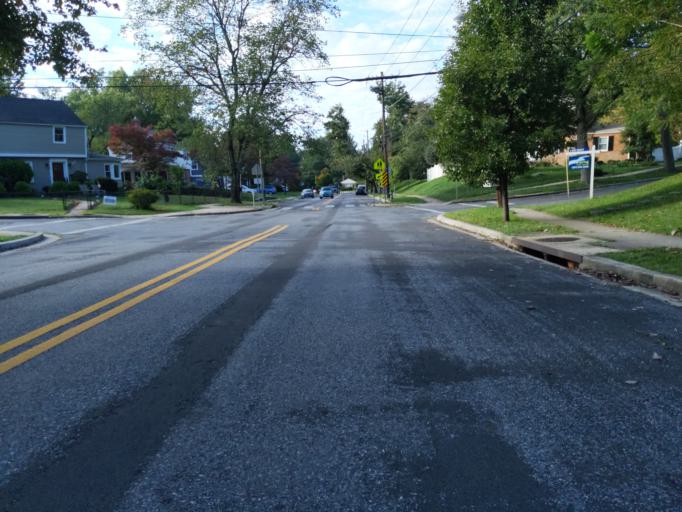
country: US
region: Maryland
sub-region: Montgomery County
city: Forest Glen
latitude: 39.0216
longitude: -77.0502
